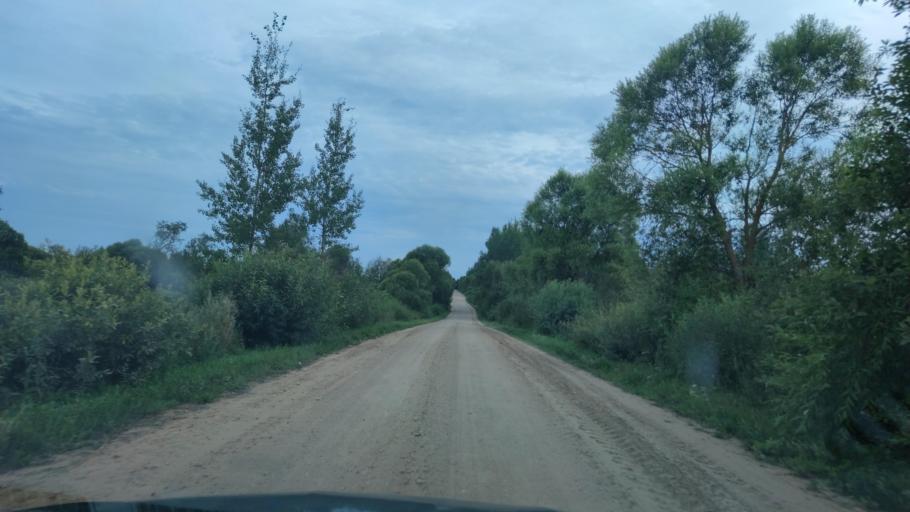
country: BY
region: Vitebsk
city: Pastavy
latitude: 55.1200
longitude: 27.1517
